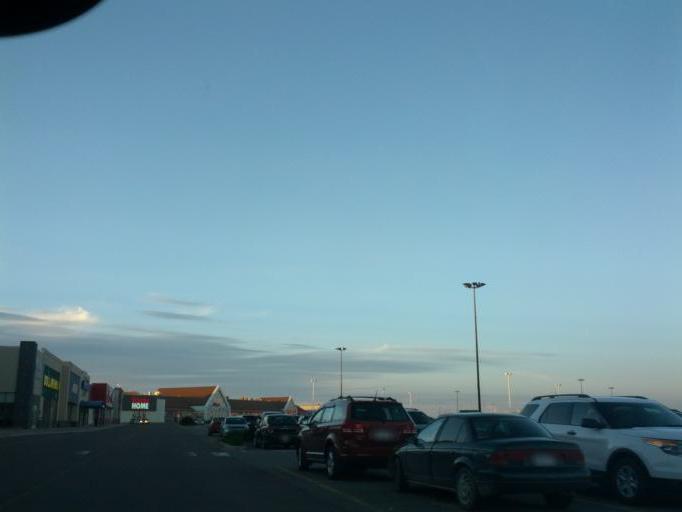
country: CA
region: New Brunswick
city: Moncton
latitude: 46.1160
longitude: -64.8342
